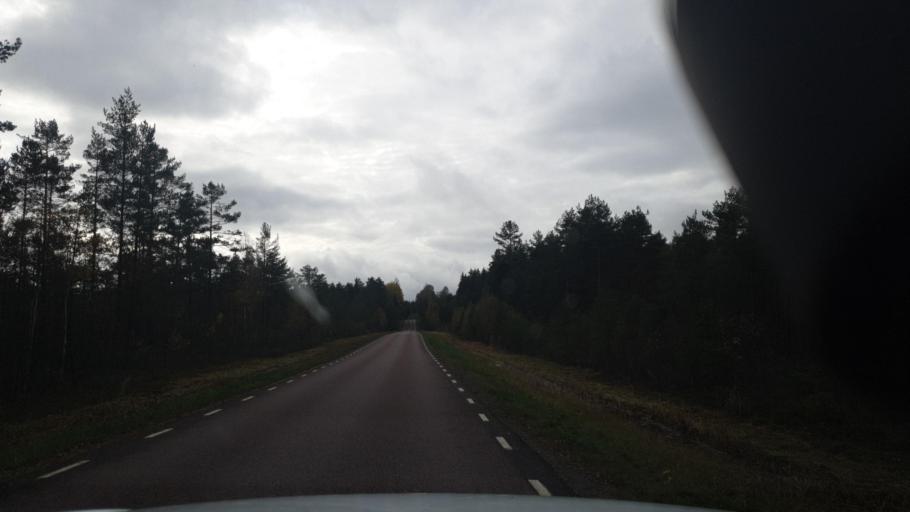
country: SE
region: Vaermland
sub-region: Karlstads Kommun
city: Edsvalla
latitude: 59.5193
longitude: 13.1117
